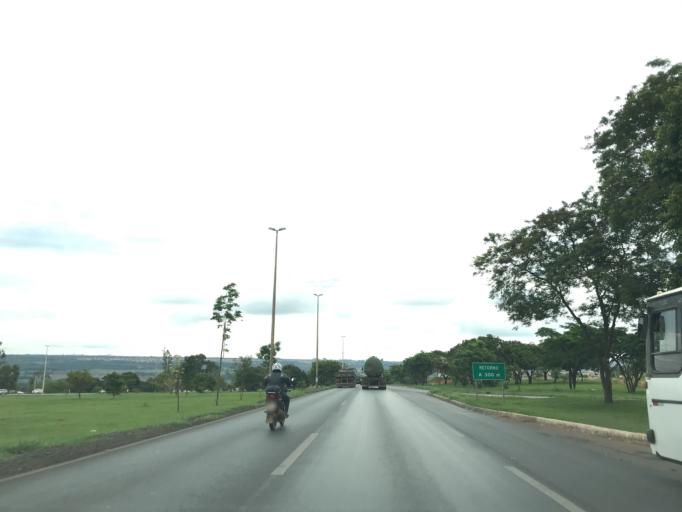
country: BR
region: Federal District
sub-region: Brasilia
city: Brasilia
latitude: -15.6537
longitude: -47.7830
